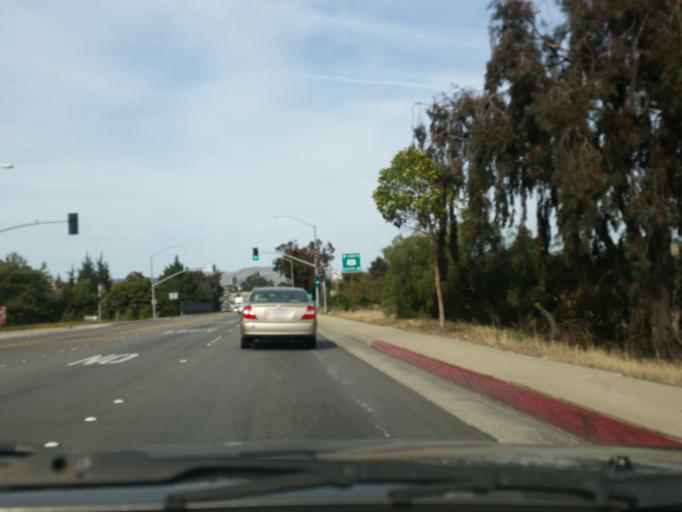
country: US
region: California
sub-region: San Luis Obispo County
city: Arroyo Grande
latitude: 35.1207
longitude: -120.5856
